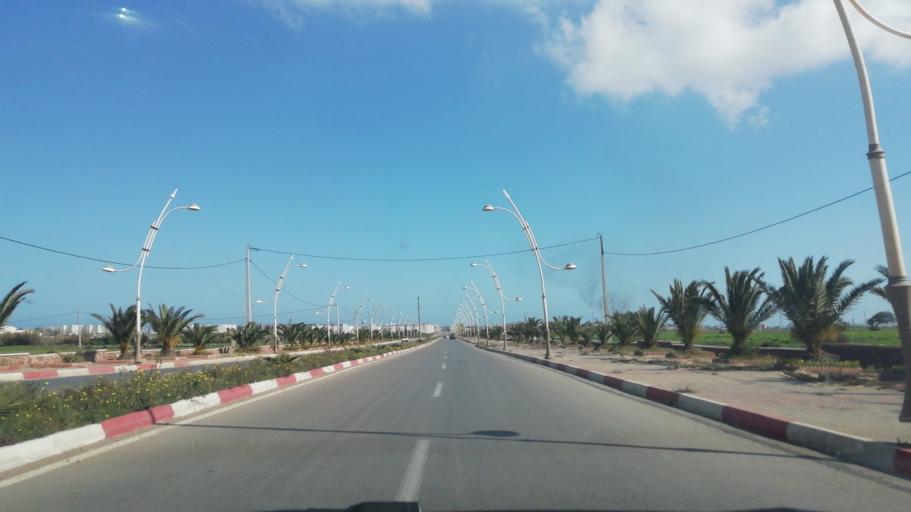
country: DZ
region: Oran
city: Ain el Bya
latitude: 35.7891
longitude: -0.2817
